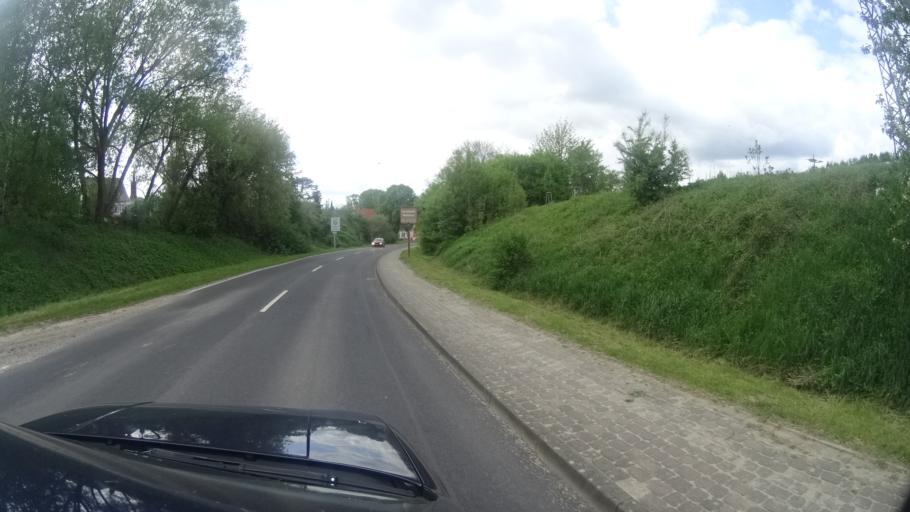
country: DE
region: Mecklenburg-Vorpommern
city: Malchow
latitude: 53.4722
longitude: 12.4371
